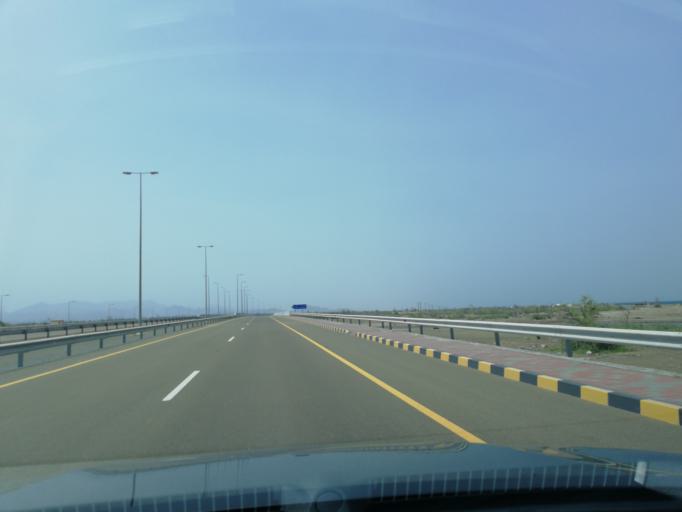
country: OM
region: Al Batinah
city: Shinas
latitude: 24.8678
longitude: 56.4102
